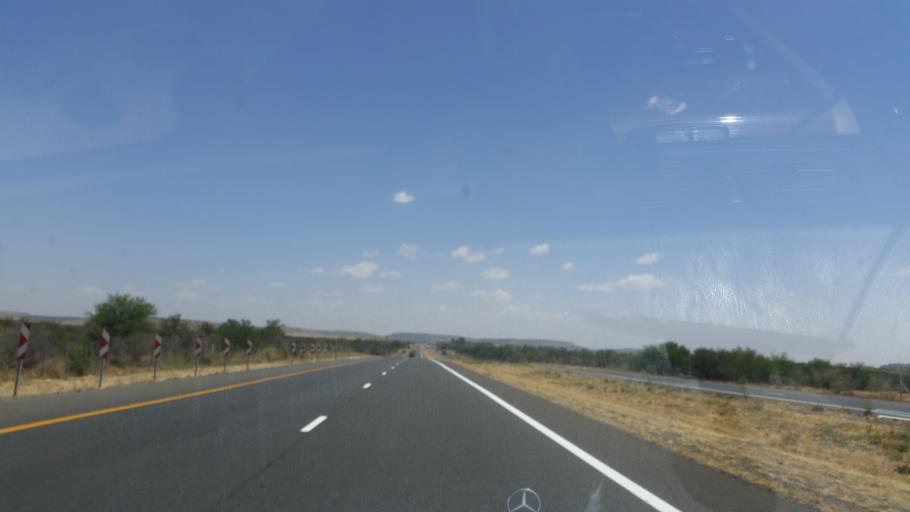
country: ZA
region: Orange Free State
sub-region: Mangaung Metropolitan Municipality
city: Bloemfontein
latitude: -28.9590
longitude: 26.3704
